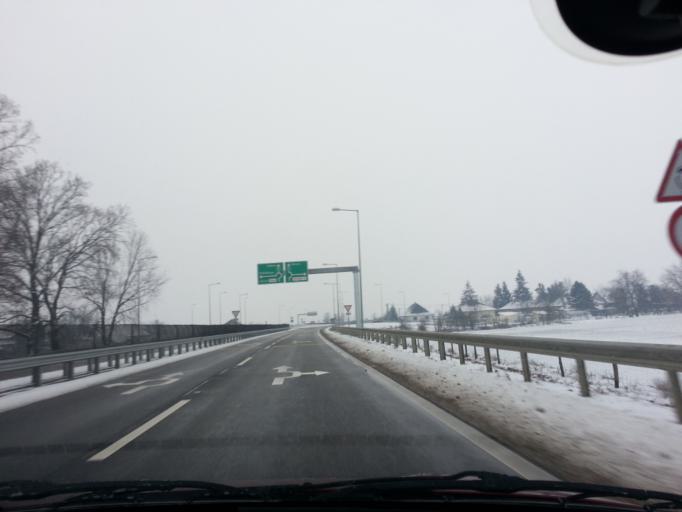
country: HU
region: Heves
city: Zagyvaszanto
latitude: 47.7629
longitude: 19.6649
